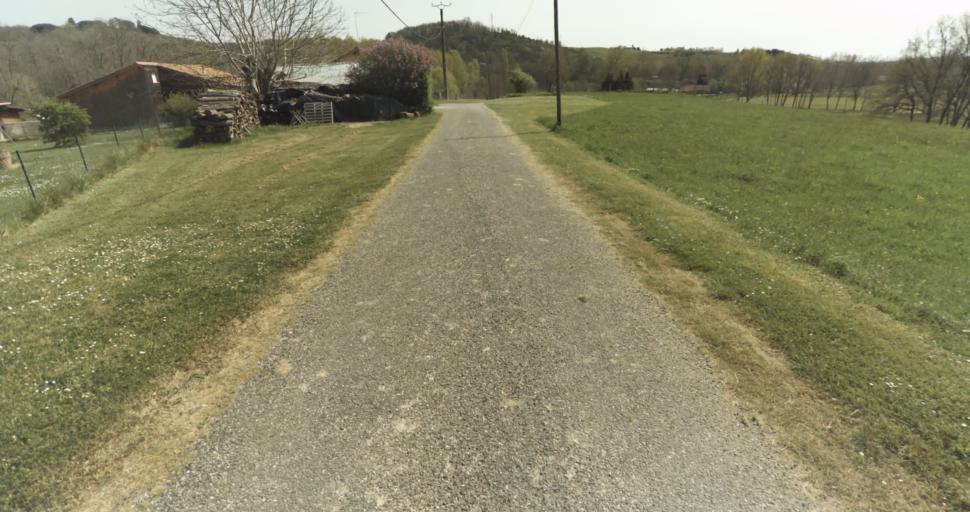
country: FR
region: Midi-Pyrenees
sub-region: Departement du Tarn-et-Garonne
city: Moissac
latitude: 44.1507
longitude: 1.1053
